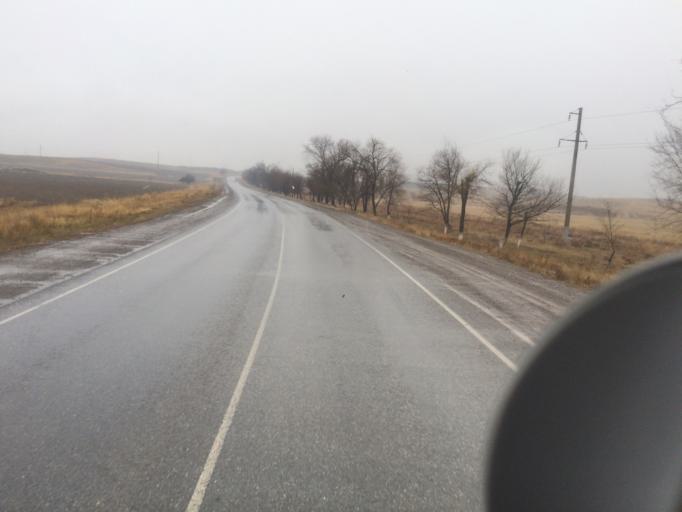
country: KG
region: Chuy
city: Kant
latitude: 43.0051
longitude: 74.8592
